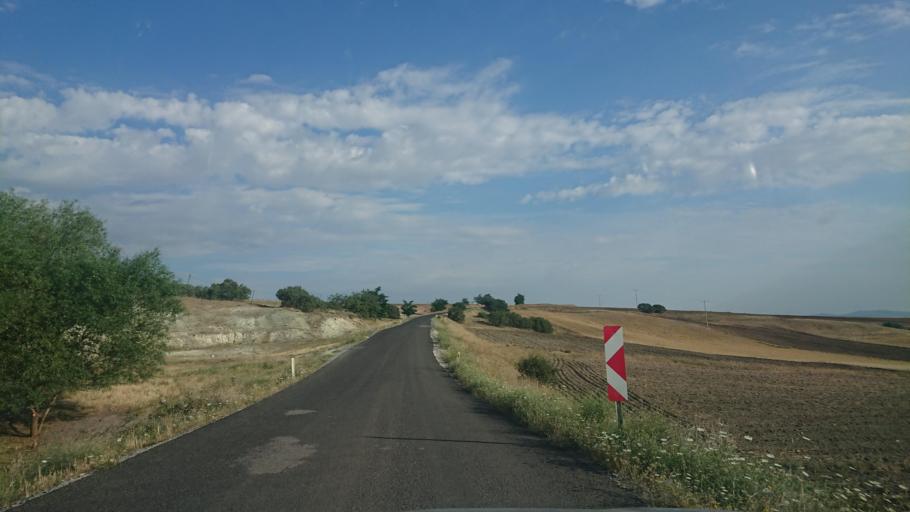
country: TR
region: Aksaray
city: Ortakoy
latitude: 38.8094
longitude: 34.0565
